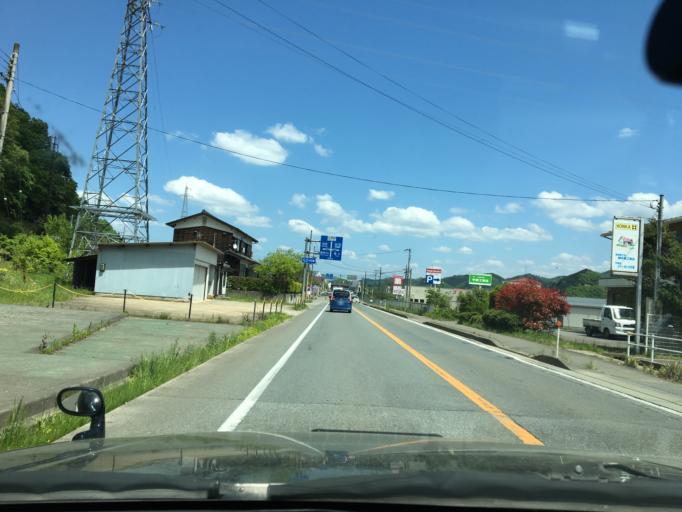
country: JP
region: Hyogo
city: Toyooka
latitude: 35.4689
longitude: 134.7652
